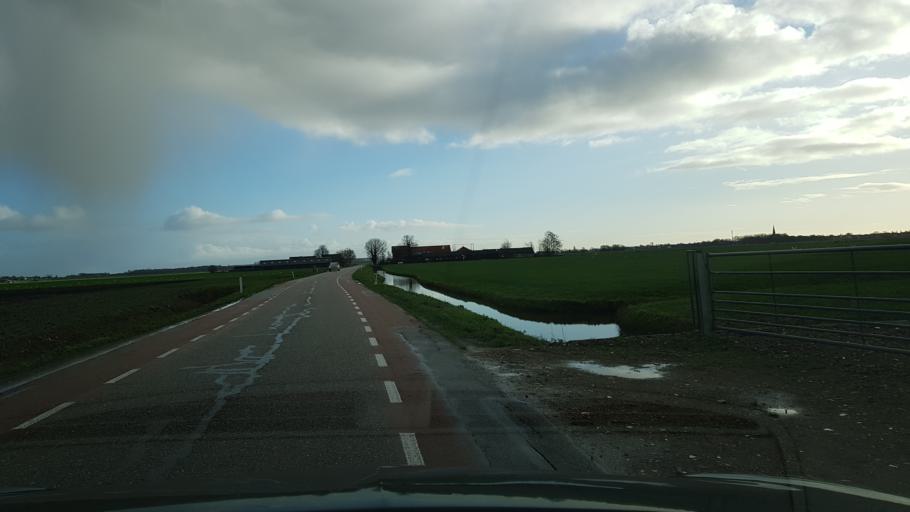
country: NL
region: South Holland
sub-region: Gemeente Kaag en Braassem
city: Leimuiden
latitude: 52.2099
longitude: 4.6880
